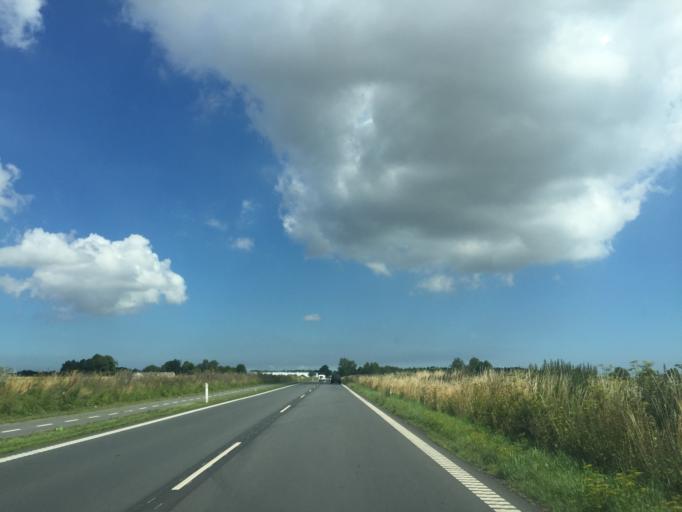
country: DK
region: South Denmark
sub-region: Nordfyns Kommune
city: Otterup
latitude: 55.4956
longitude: 10.3855
